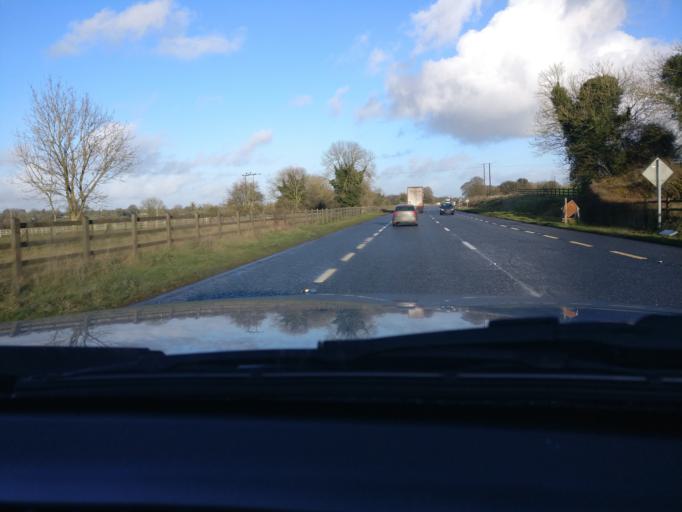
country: IE
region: Leinster
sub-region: An Iarmhi
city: Rathwire
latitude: 53.5904
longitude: -7.1240
